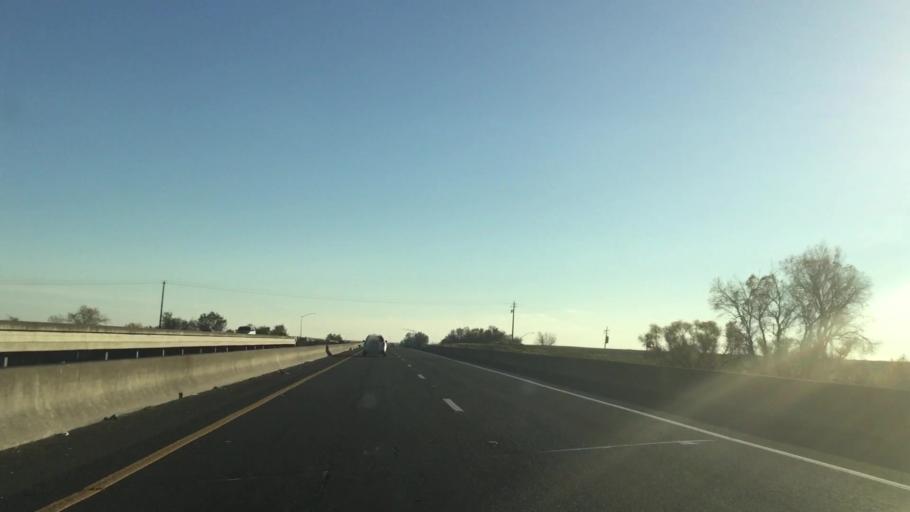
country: US
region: California
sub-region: Sacramento County
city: Elverta
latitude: 38.8220
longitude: -121.5438
